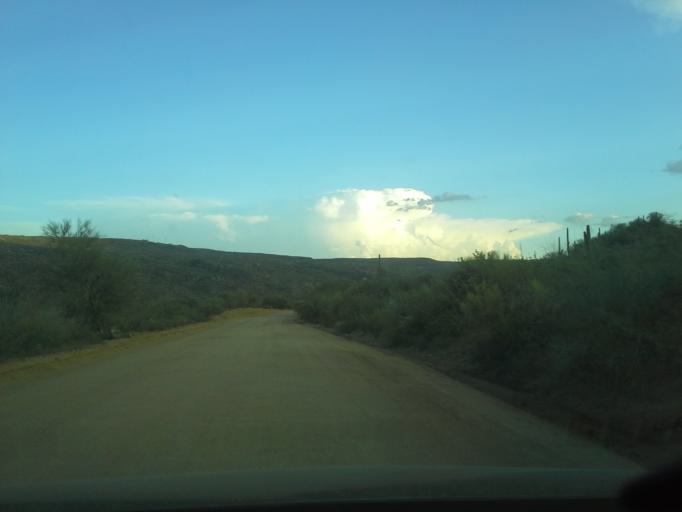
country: US
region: Arizona
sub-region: Yavapai County
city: Cordes Lakes
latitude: 34.2134
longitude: -112.1484
